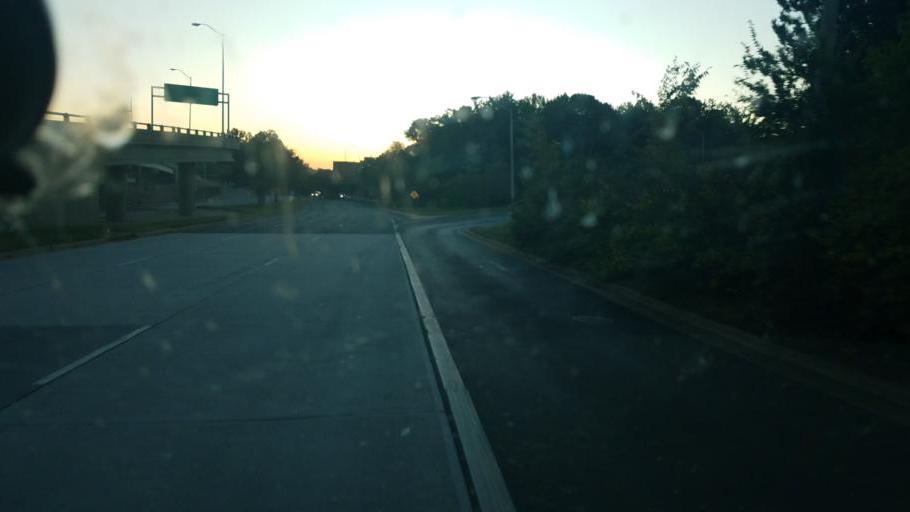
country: US
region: Virginia
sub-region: Fairfax County
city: Lincolnia
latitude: 38.8140
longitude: -77.1324
